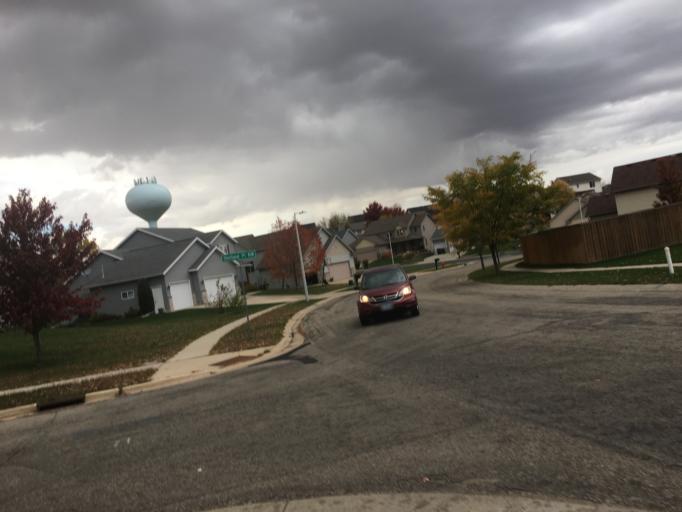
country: US
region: Minnesota
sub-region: Olmsted County
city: Oronoco
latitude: 44.0884
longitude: -92.5273
